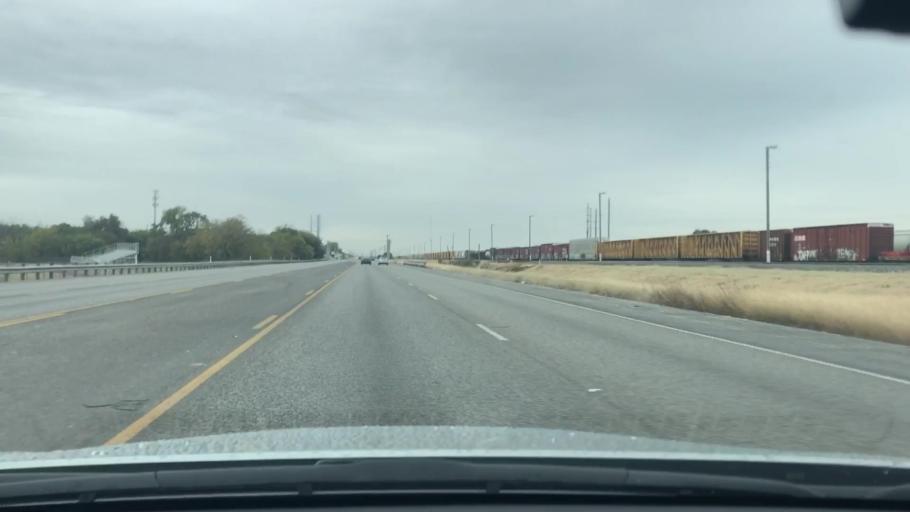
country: US
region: Texas
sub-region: Bexar County
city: Kirby
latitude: 29.4705
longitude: -98.3882
